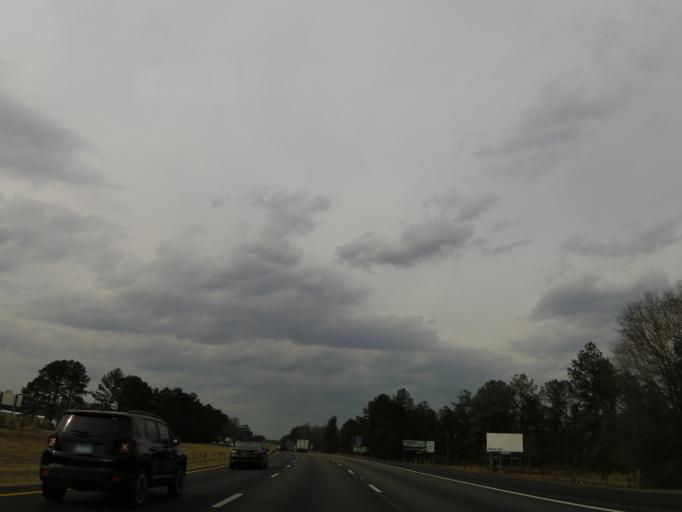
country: US
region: South Carolina
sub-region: Lexington County
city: Pineridge
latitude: 33.8864
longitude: -81.0380
